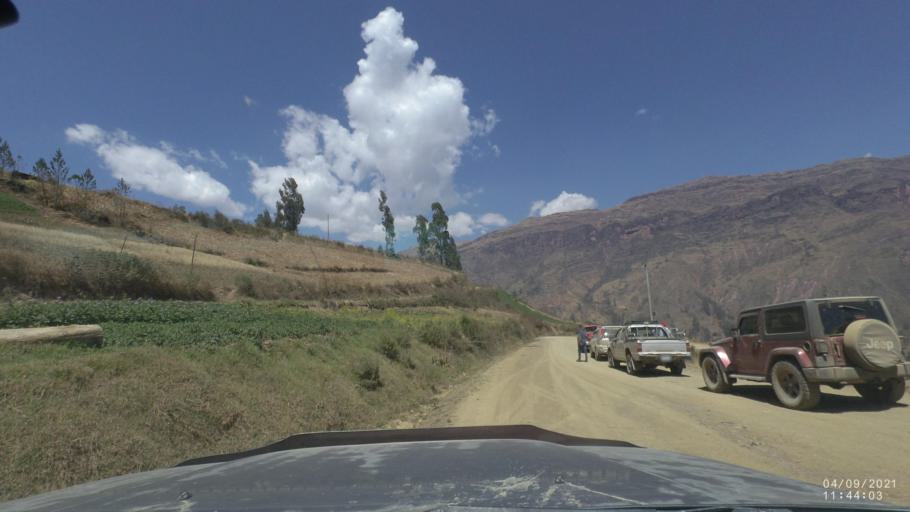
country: BO
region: Cochabamba
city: Colchani
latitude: -17.2270
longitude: -66.5232
